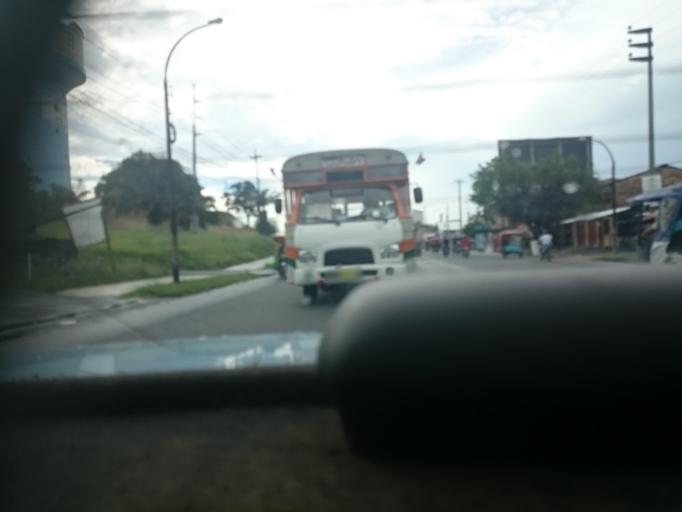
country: PE
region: Loreto
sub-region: Provincia de Maynas
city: Iquitos
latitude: -3.7649
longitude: -73.2587
